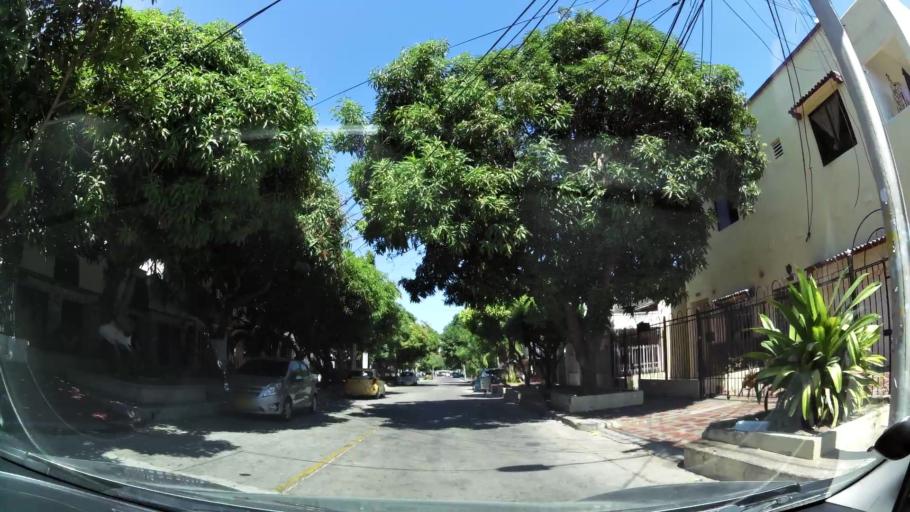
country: CO
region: Atlantico
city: Barranquilla
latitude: 10.9881
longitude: -74.7971
